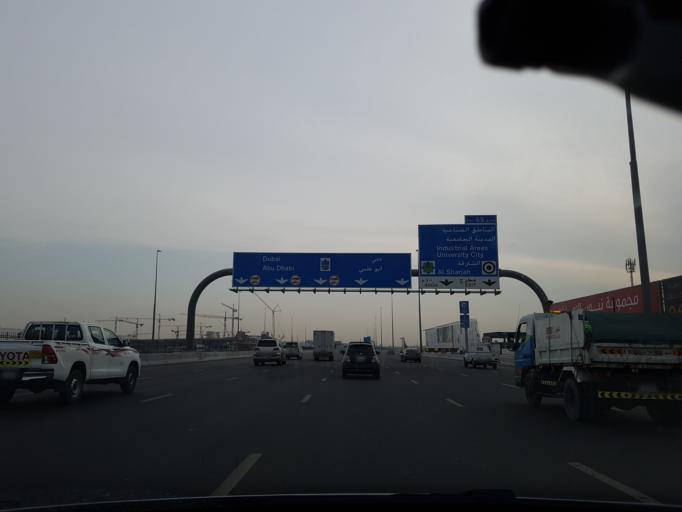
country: AE
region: Ash Shariqah
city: Sharjah
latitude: 25.3252
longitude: 55.4583
